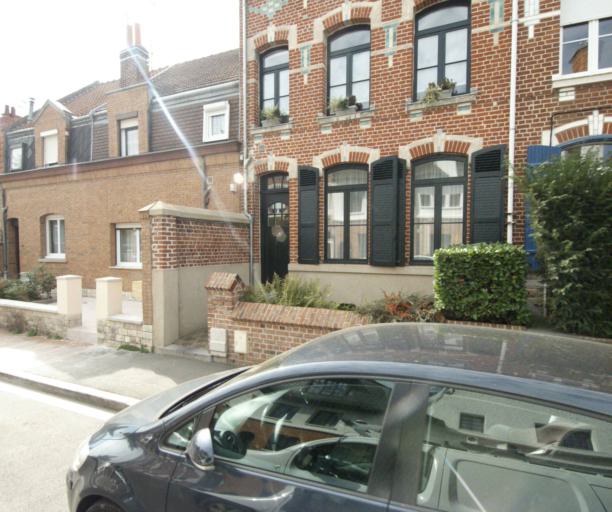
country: FR
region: Nord-Pas-de-Calais
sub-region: Departement du Nord
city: Templemars
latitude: 50.5758
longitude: 3.0531
